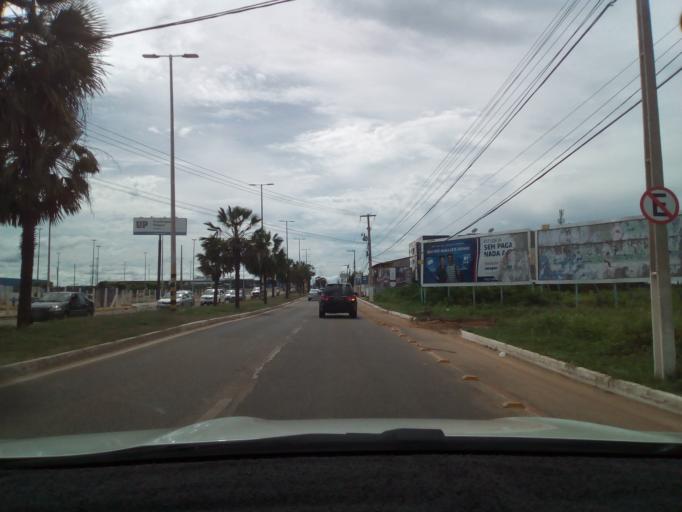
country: BR
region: Rio Grande do Norte
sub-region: Mossoro
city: Mossoro
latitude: -5.1760
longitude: -37.3691
